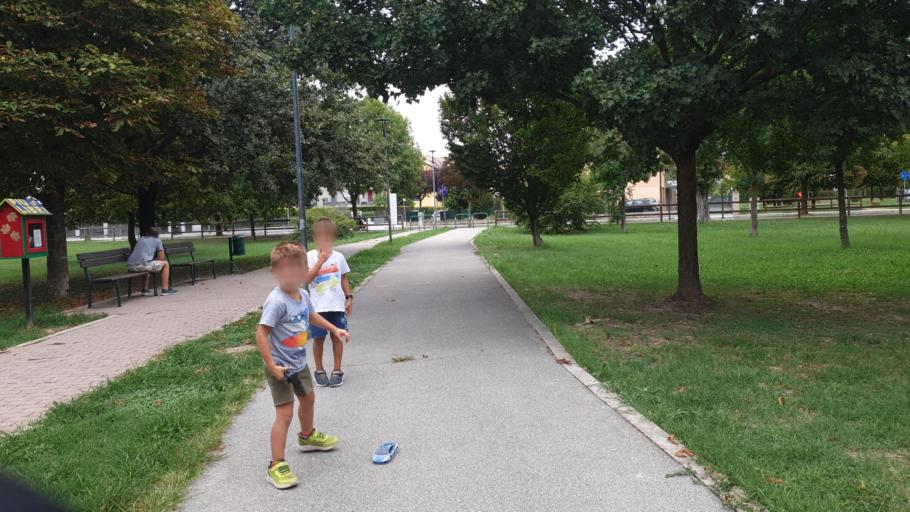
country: IT
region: Veneto
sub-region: Provincia di Padova
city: Mandriola-Sant'Agostino
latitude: 45.3486
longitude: 11.8592
